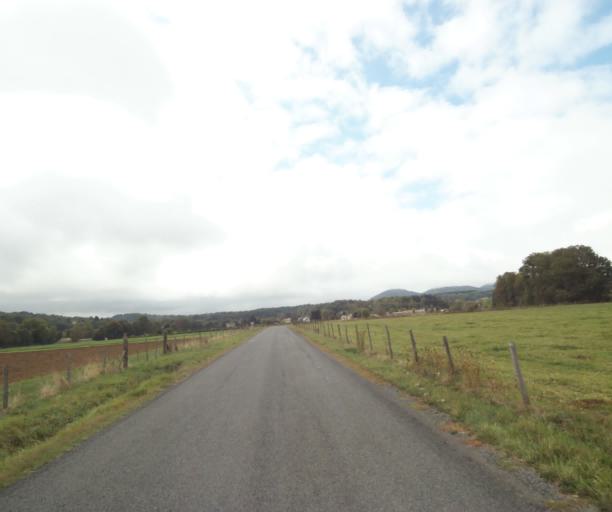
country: FR
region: Auvergne
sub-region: Departement du Puy-de-Dome
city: Saint-Genes-Champanelle
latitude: 45.7073
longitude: 3.0097
